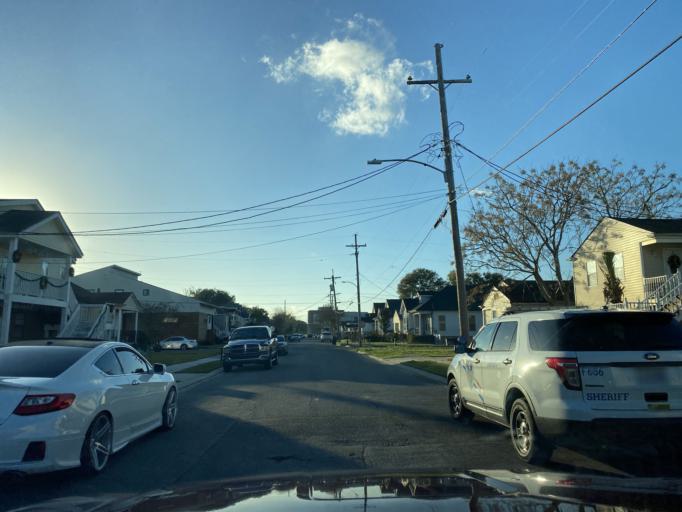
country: US
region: Louisiana
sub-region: Orleans Parish
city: New Orleans
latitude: 30.0183
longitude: -90.0532
